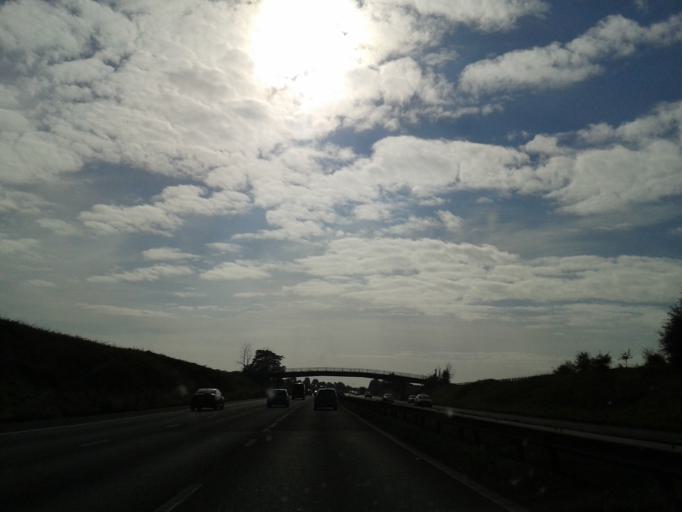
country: GB
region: England
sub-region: Cheshire East
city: Holmes Chapel
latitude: 53.1809
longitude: -2.3678
